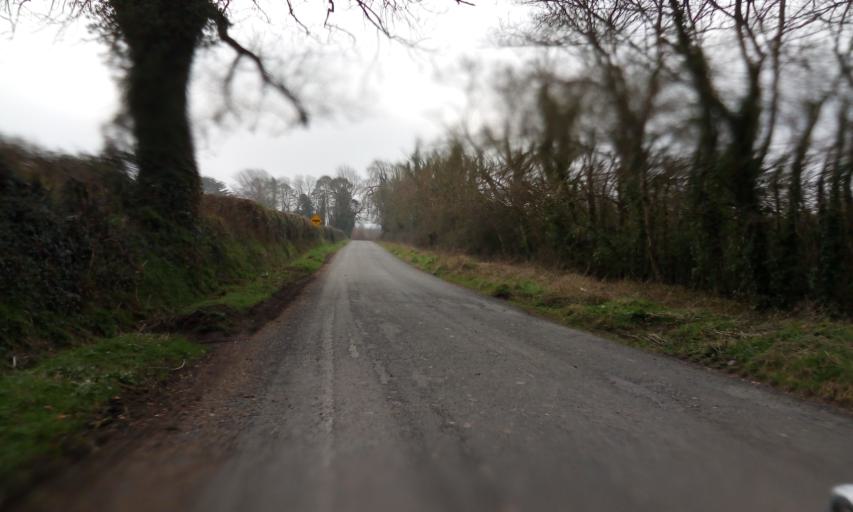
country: IE
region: Leinster
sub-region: Kilkenny
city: Kilkenny
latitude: 52.6614
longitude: -7.1879
